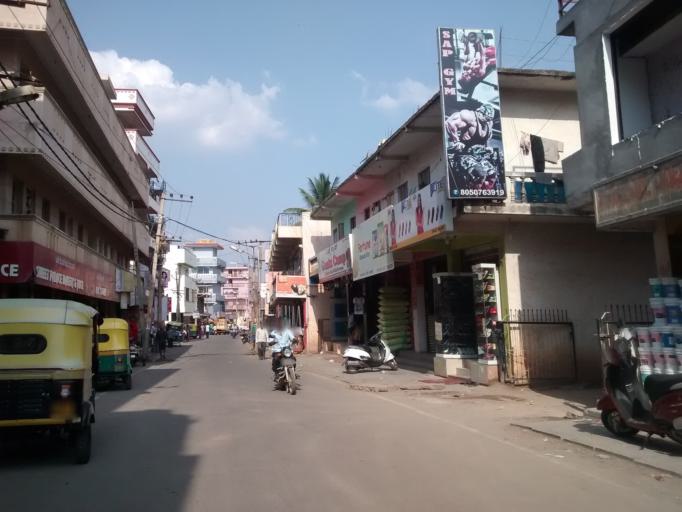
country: IN
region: Karnataka
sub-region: Bangalore Urban
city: Bangalore
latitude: 12.9647
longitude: 77.6747
